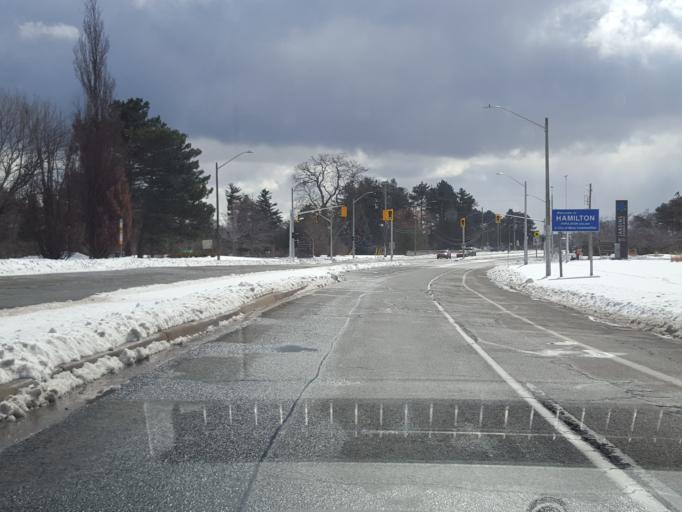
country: CA
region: Ontario
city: Hamilton
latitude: 43.2902
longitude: -79.8905
